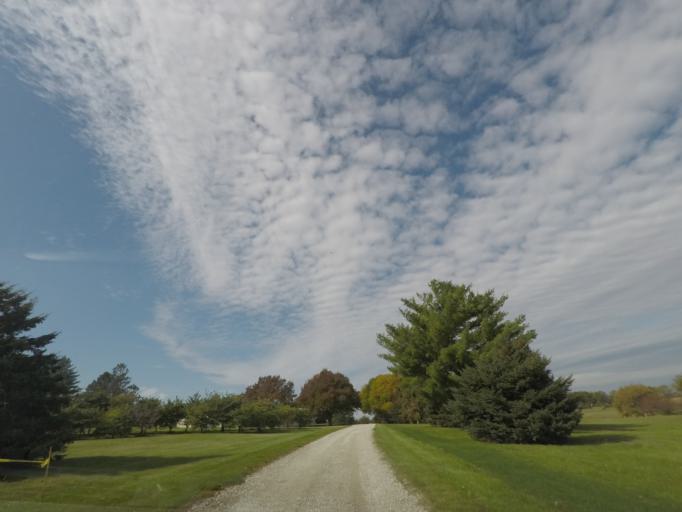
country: US
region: Iowa
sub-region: Story County
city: Gilbert
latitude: 42.1091
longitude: -93.5865
